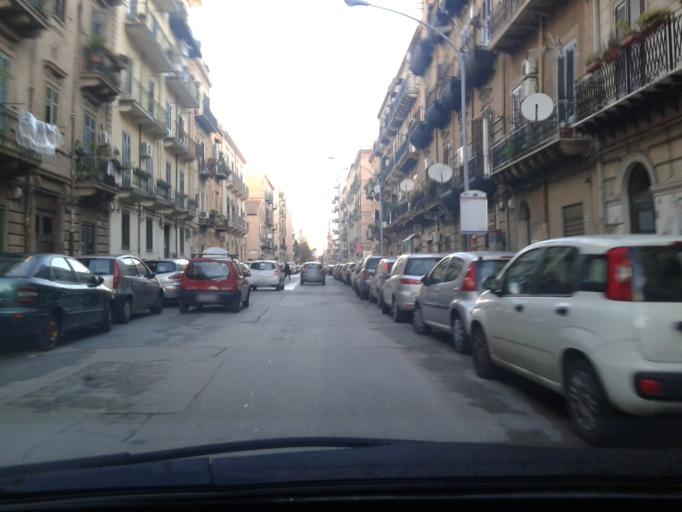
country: IT
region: Sicily
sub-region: Palermo
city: Palermo
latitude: 38.1206
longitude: 13.3453
